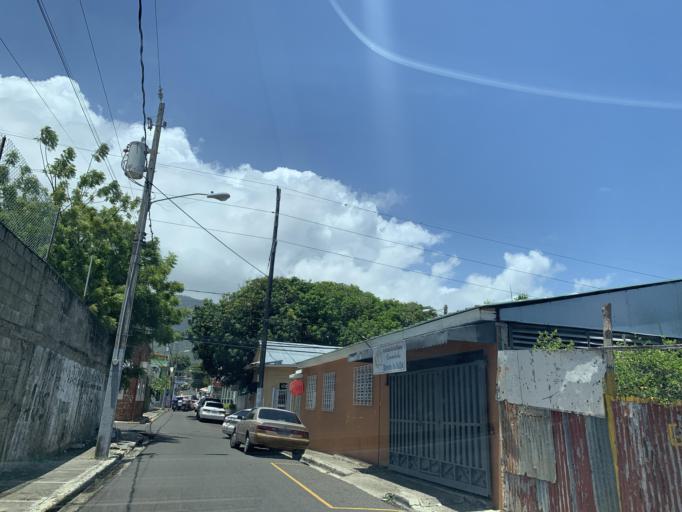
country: DO
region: Puerto Plata
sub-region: Puerto Plata
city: Puerto Plata
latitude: 19.7973
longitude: -70.6902
